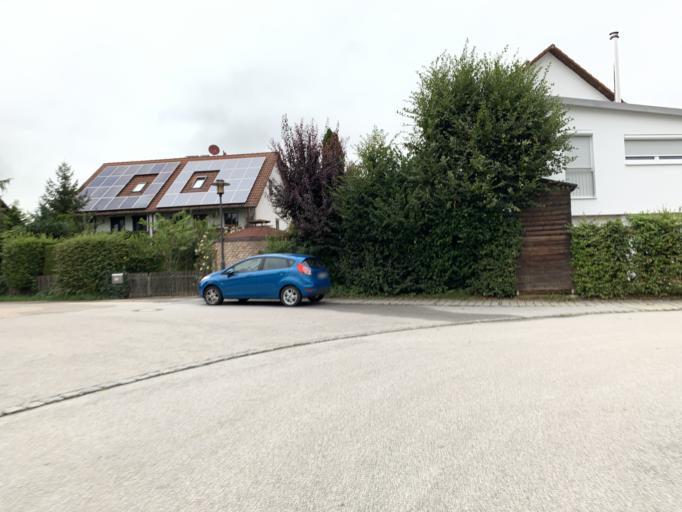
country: DE
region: Bavaria
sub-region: Upper Bavaria
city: Marzling
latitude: 48.4097
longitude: 11.8007
